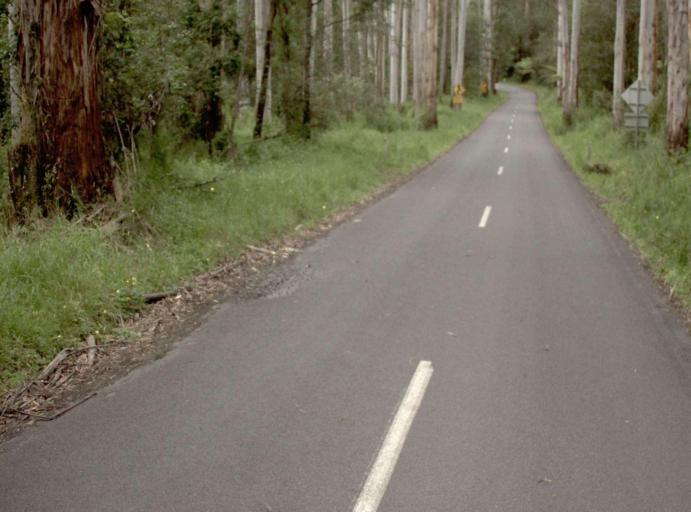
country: AU
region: Victoria
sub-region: Baw Baw
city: Warragul
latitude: -37.9069
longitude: 146.1013
